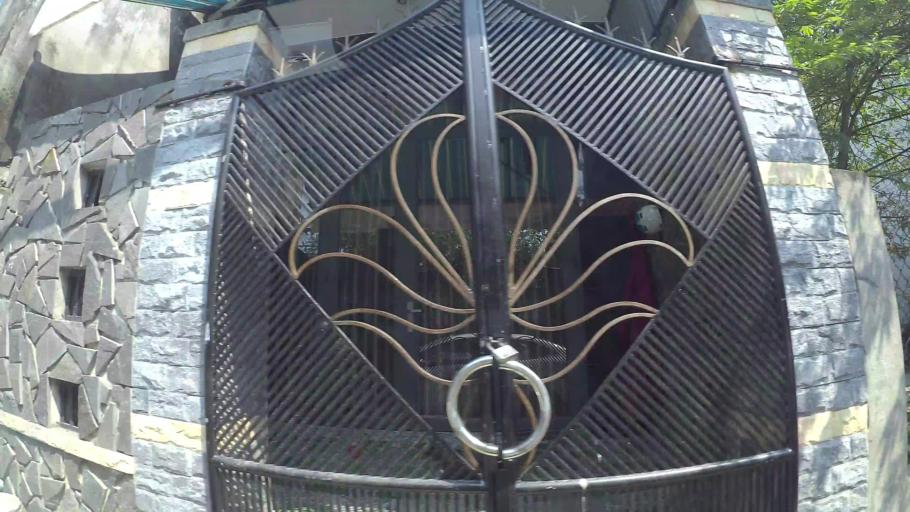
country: VN
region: Da Nang
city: Cam Le
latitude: 16.0114
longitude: 108.2032
